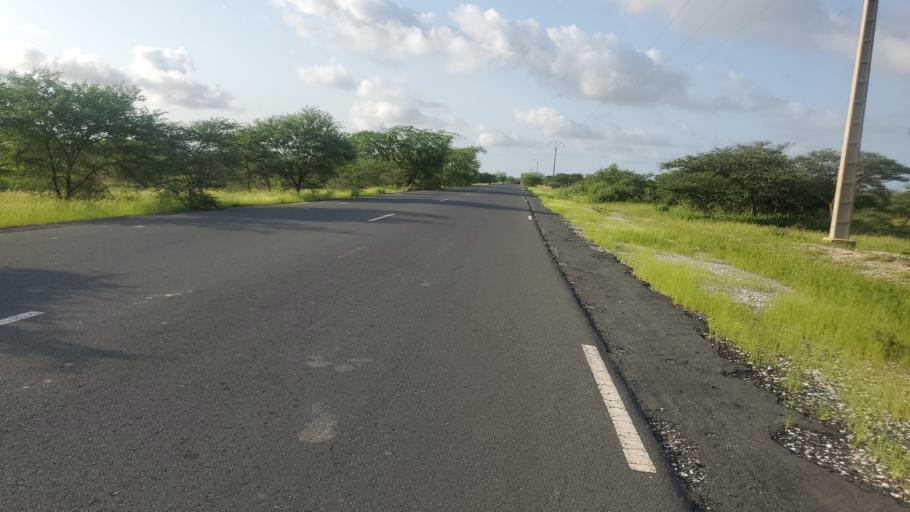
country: SN
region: Saint-Louis
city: Saint-Louis
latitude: 16.1141
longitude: -16.4134
